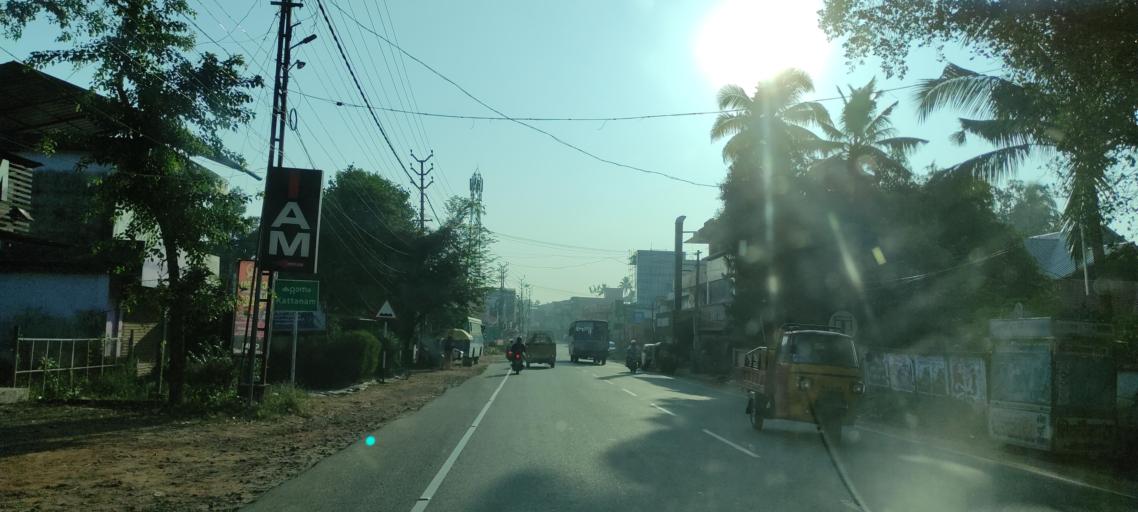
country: IN
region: Kerala
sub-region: Alappuzha
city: Kattanam
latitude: 9.1767
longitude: 76.5617
